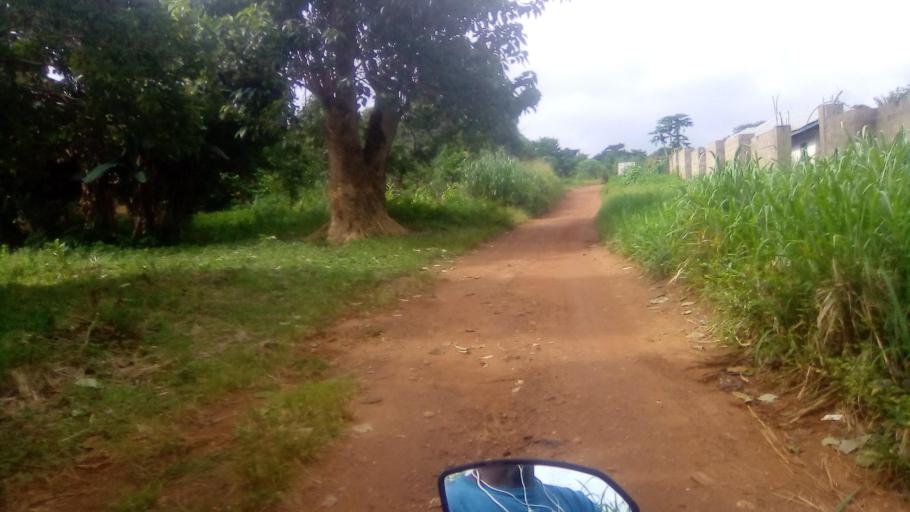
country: SL
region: Eastern Province
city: Kailahun
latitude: 8.2655
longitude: -10.5626
